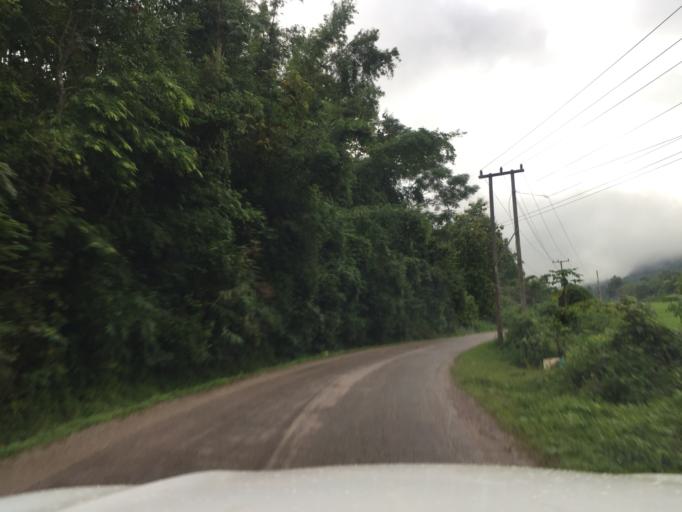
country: LA
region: Oudomxai
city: Muang La
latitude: 20.8470
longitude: 102.1059
